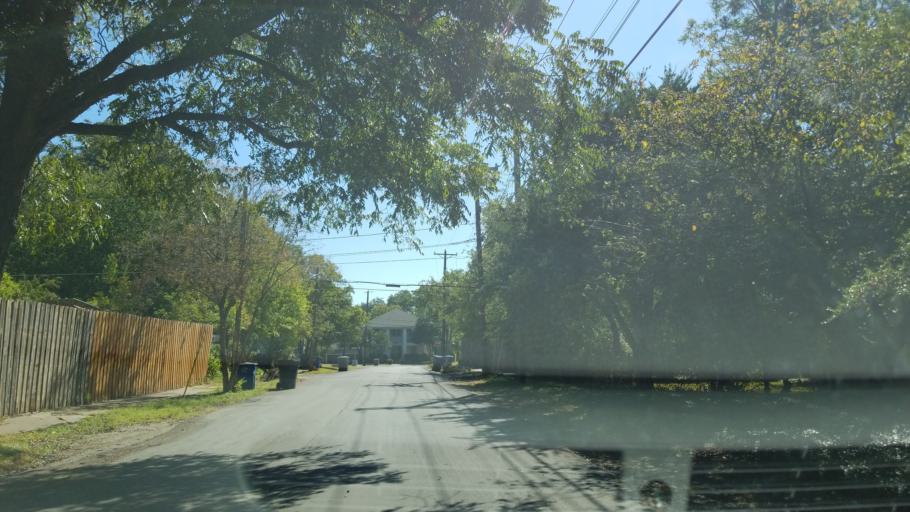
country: US
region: Texas
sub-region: Dallas County
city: Highland Park
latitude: 32.8058
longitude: -96.7542
